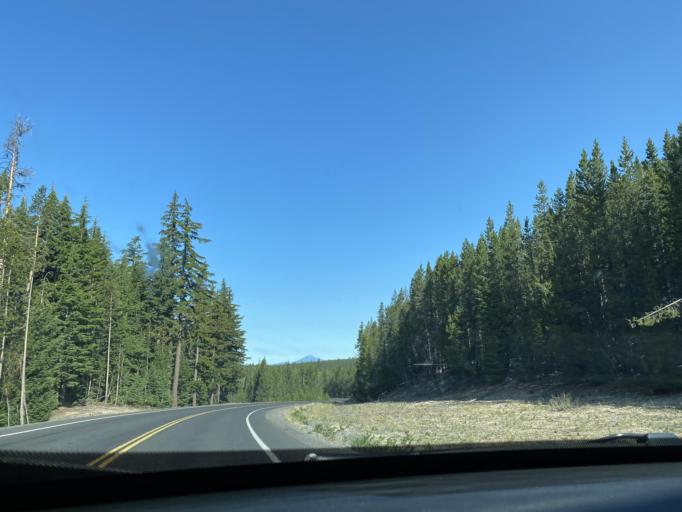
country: US
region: Oregon
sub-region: Deschutes County
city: Three Rivers
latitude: 43.7048
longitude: -121.2639
